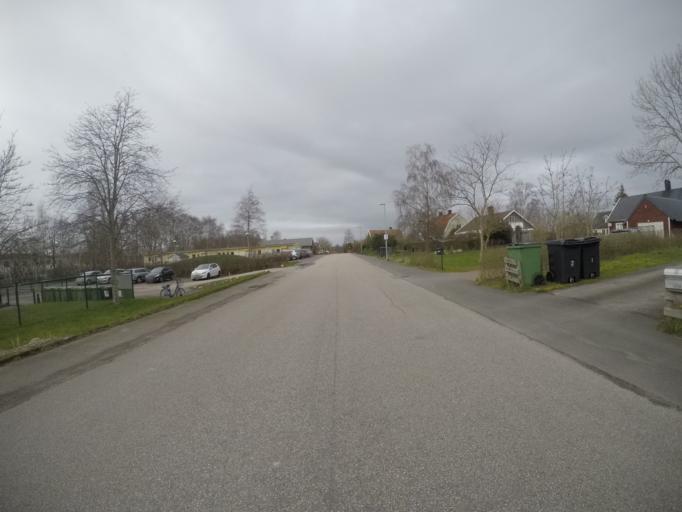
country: SE
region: Halland
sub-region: Laholms Kommun
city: Laholm
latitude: 56.5082
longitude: 13.0531
